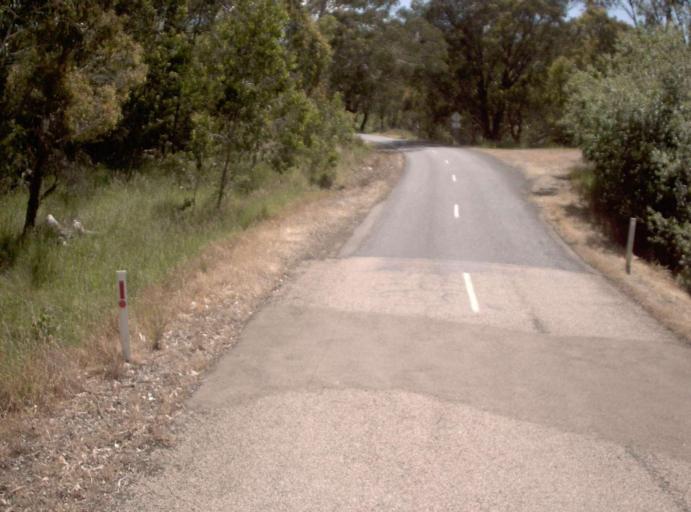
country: AU
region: New South Wales
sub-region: Bombala
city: Bombala
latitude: -37.0609
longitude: 148.8006
